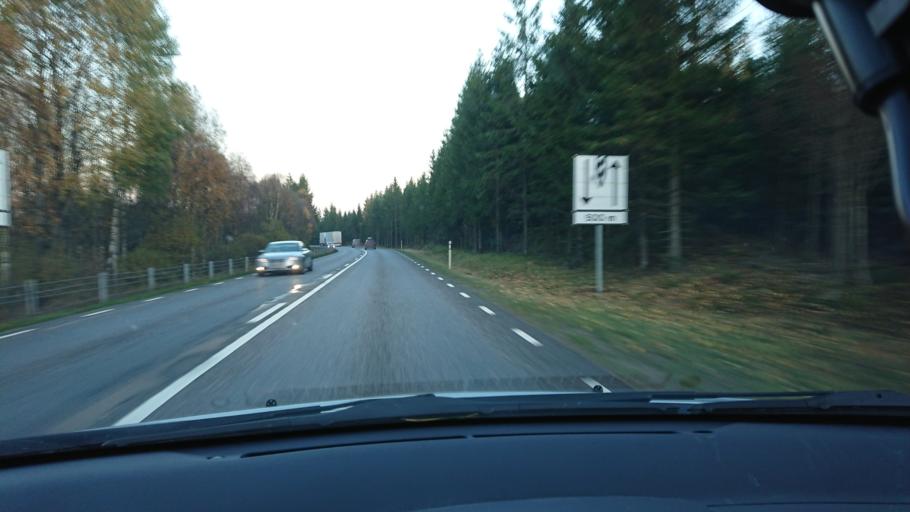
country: SE
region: Halland
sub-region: Laholms Kommun
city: Knared
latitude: 56.7179
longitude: 13.3109
